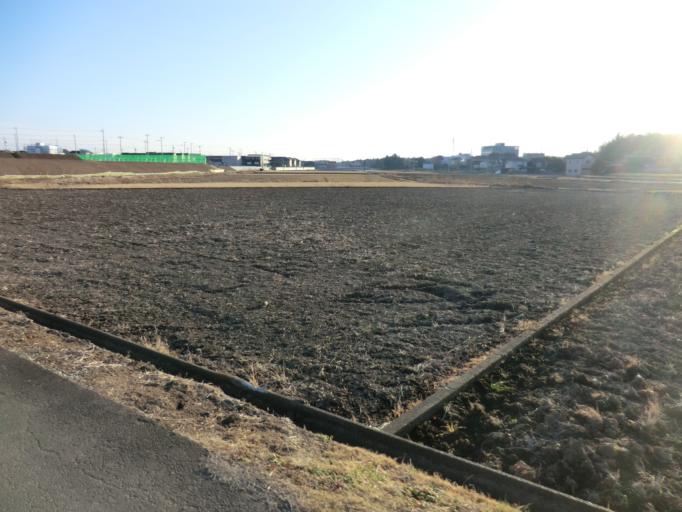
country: JP
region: Ibaraki
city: Naka
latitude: 36.0904
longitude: 140.0718
